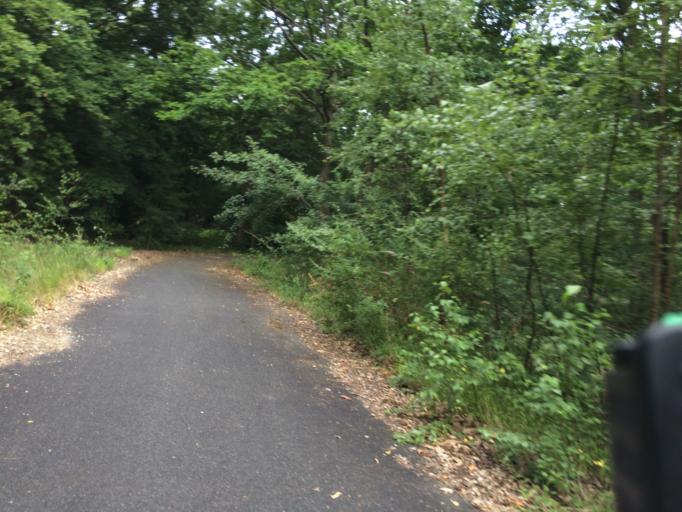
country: FR
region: Ile-de-France
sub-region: Departement de l'Essonne
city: Soisy-sur-Seine
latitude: 48.6646
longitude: 2.4454
